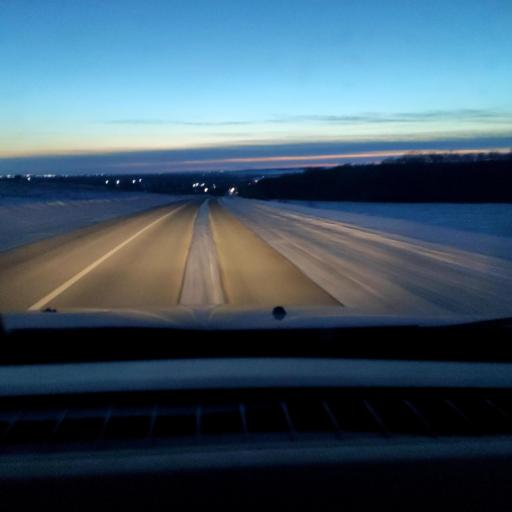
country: RU
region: Samara
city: Kinel'
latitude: 53.3026
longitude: 50.7915
